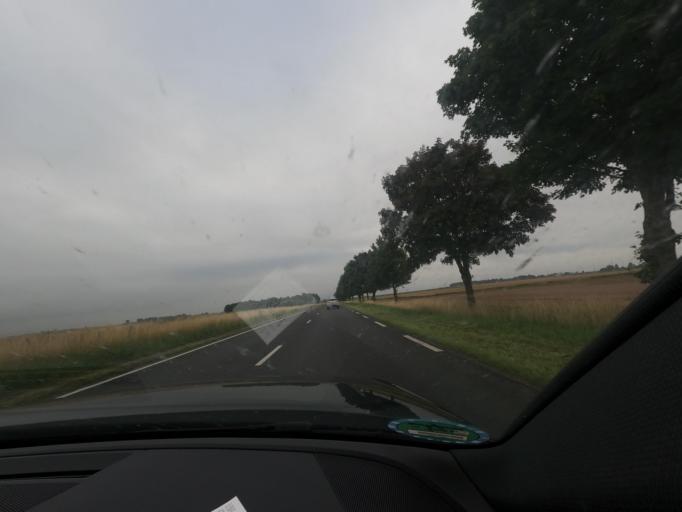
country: FR
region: Picardie
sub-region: Departement de la Somme
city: Rosieres-en-Santerre
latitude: 49.7640
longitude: 2.6315
